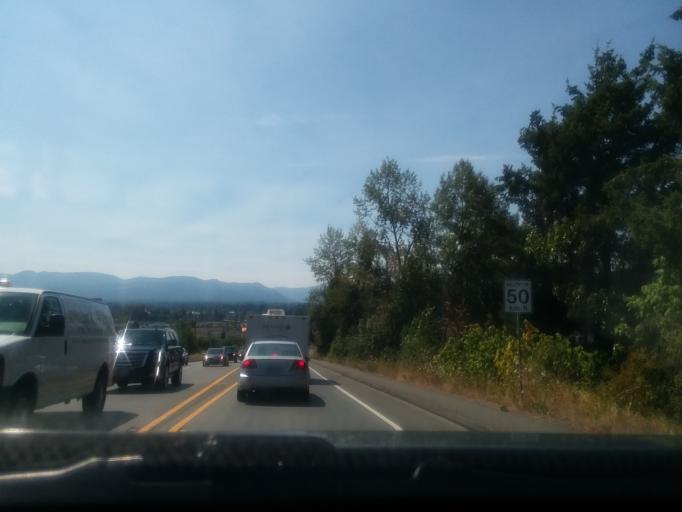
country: CA
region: British Columbia
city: Courtenay
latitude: 49.7027
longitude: -124.9804
